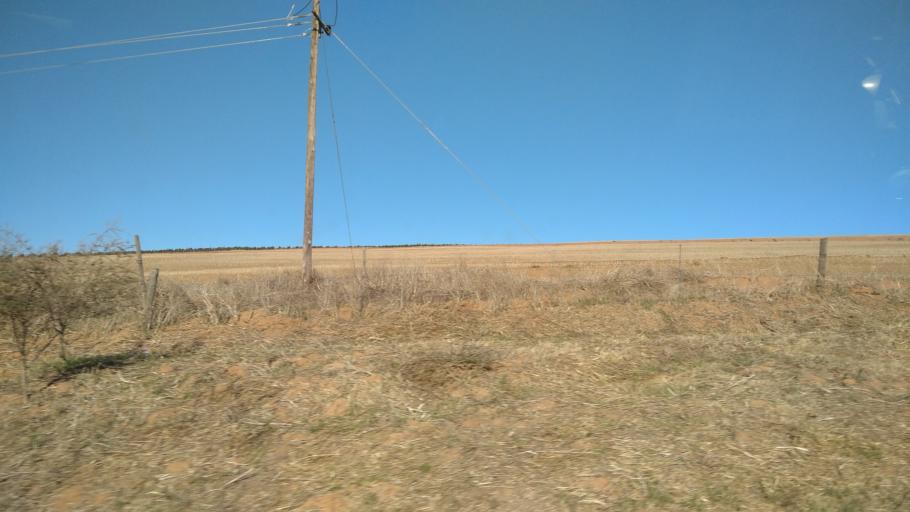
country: ZA
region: Western Cape
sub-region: West Coast District Municipality
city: Malmesbury
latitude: -33.4021
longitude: 18.6924
